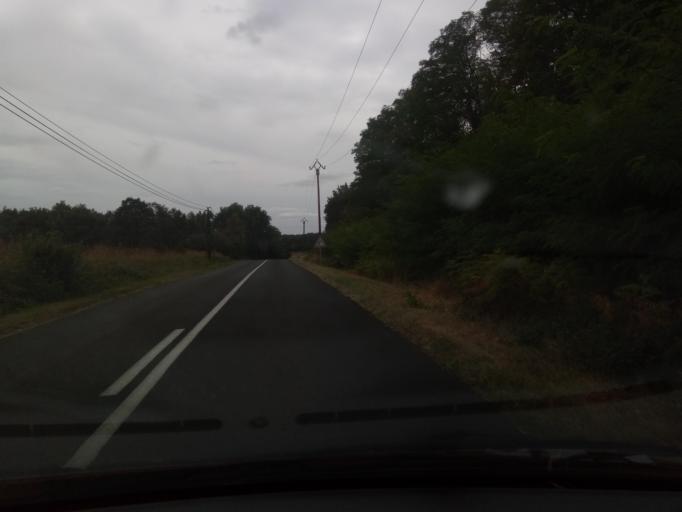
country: FR
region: Poitou-Charentes
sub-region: Departement de la Vienne
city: Pleumartin
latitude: 46.6763
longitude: 0.8260
